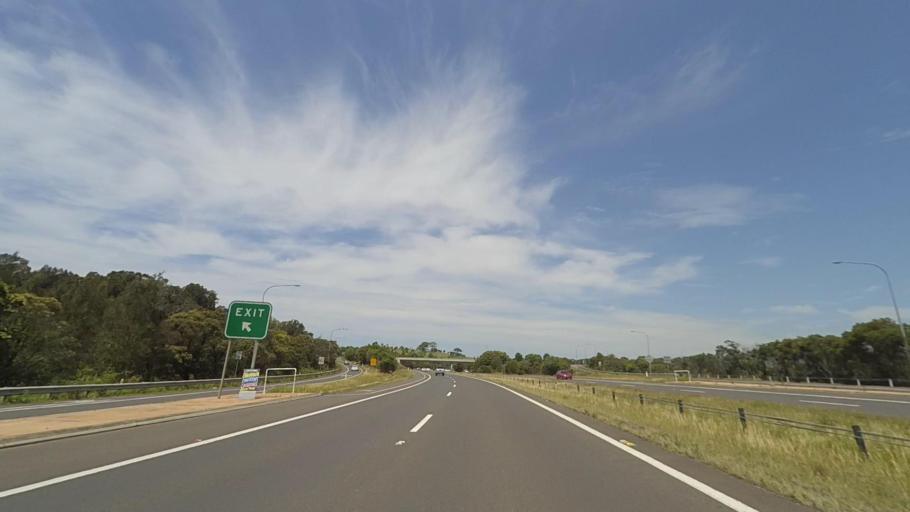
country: AU
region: New South Wales
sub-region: Shellharbour
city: Croom
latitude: -34.6140
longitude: 150.8372
